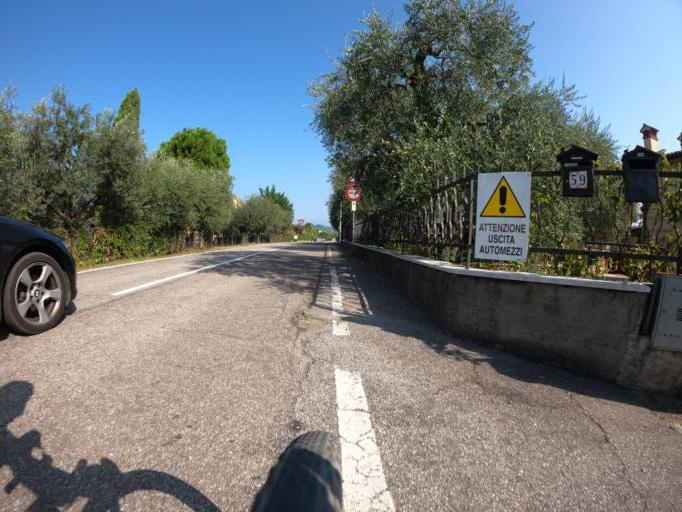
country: IT
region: Veneto
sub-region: Provincia di Verona
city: Bardolino
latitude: 45.5270
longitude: 10.7350
